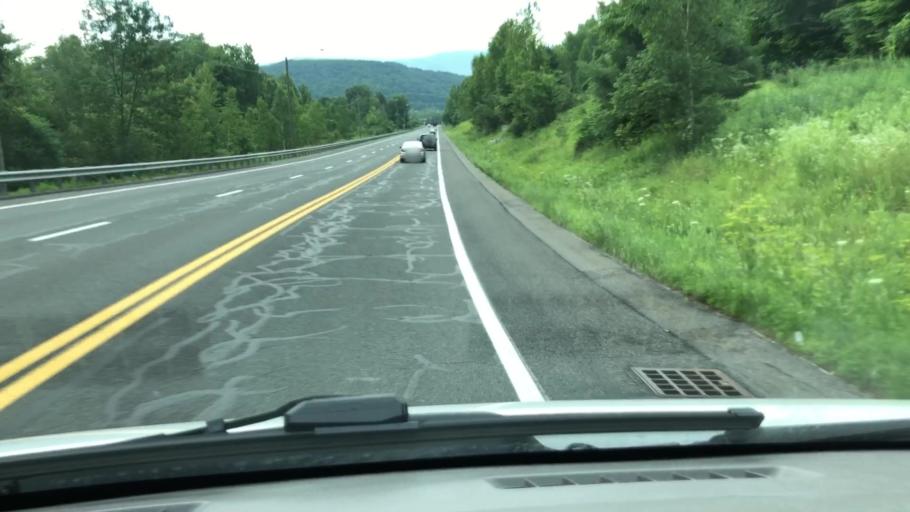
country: US
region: Massachusetts
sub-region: Berkshire County
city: Lanesborough
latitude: 42.4950
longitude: -73.2179
